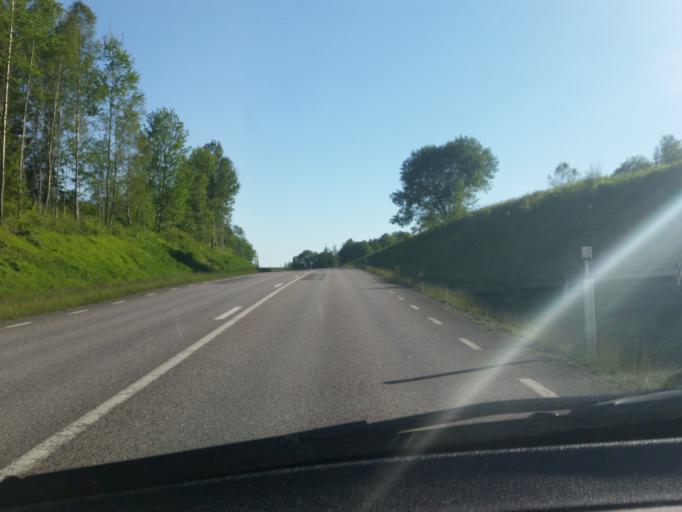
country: SE
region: Vaestra Goetaland
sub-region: Fargelanda Kommun
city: Faergelanda
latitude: 58.5769
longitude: 12.0108
